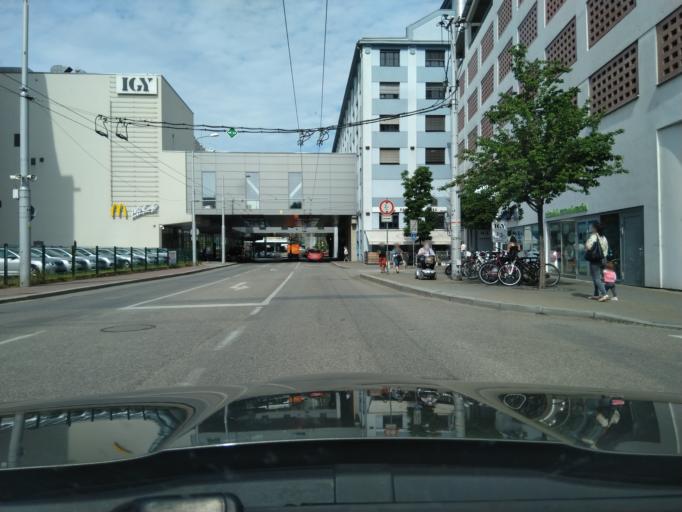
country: CZ
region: Jihocesky
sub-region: Okres Ceske Budejovice
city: Ceske Budejovice
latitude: 48.9837
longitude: 14.4740
